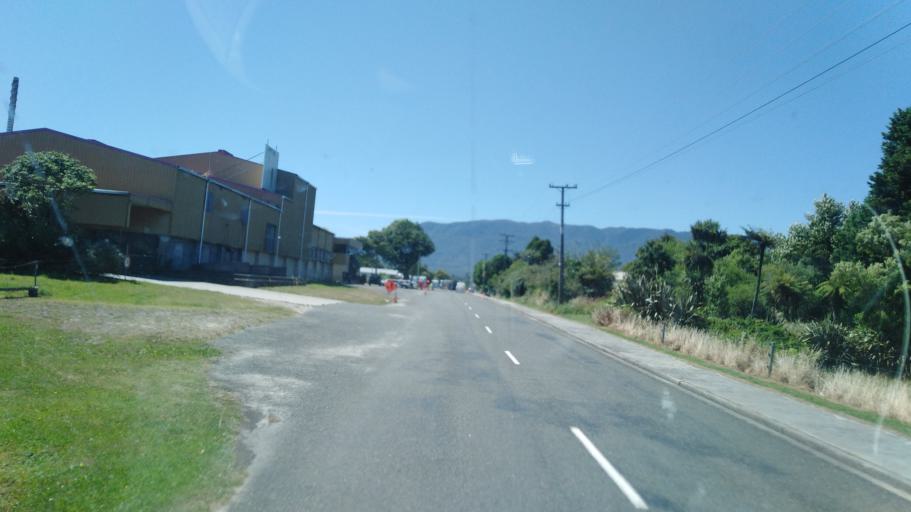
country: NZ
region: West Coast
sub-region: Buller District
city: Westport
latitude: -41.2504
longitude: 172.1261
